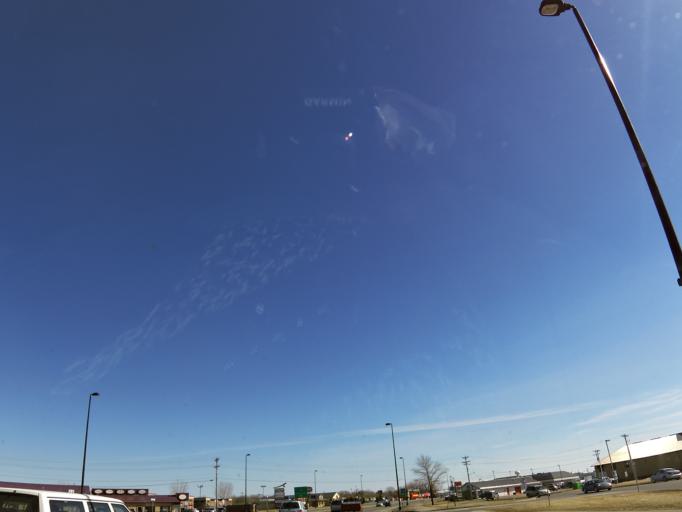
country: US
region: Minnesota
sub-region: Wright County
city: Buffalo
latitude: 45.1788
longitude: -93.8696
